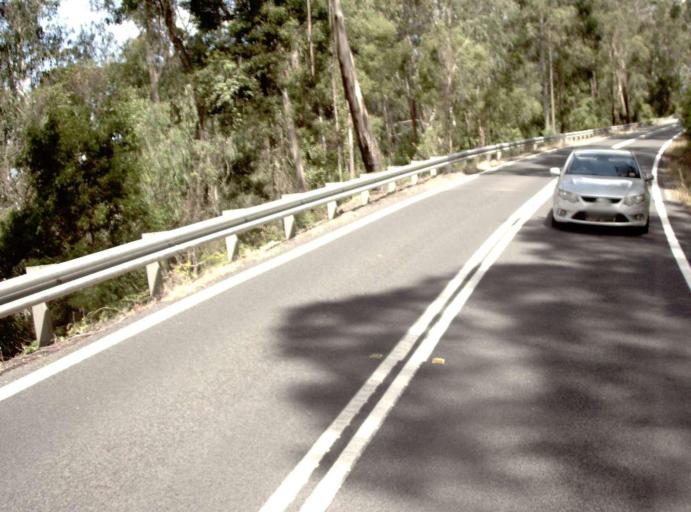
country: AU
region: New South Wales
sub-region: Bombala
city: Bombala
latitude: -37.5589
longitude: 149.3527
